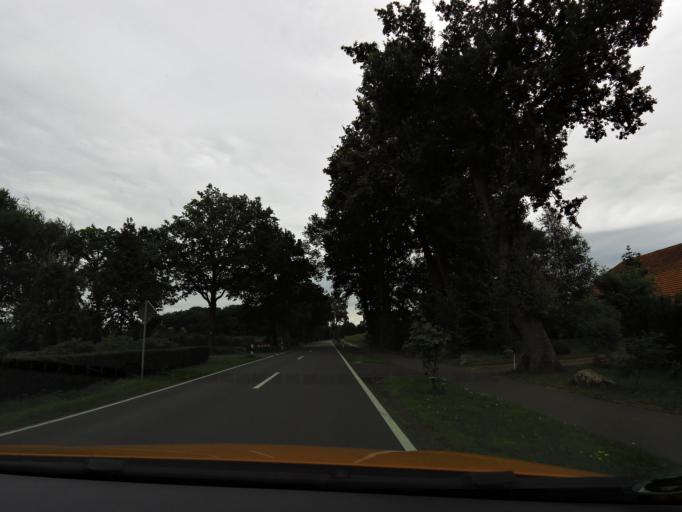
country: DE
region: Lower Saxony
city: Wiefelstede
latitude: 53.1946
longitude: 8.1375
